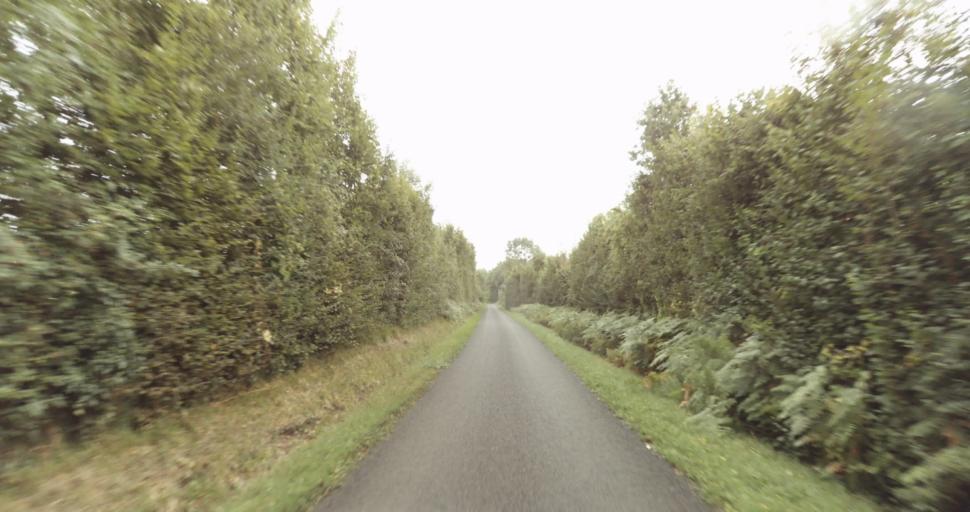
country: FR
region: Lower Normandy
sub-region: Departement de l'Orne
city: Vimoutiers
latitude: 48.8790
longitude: 0.2003
